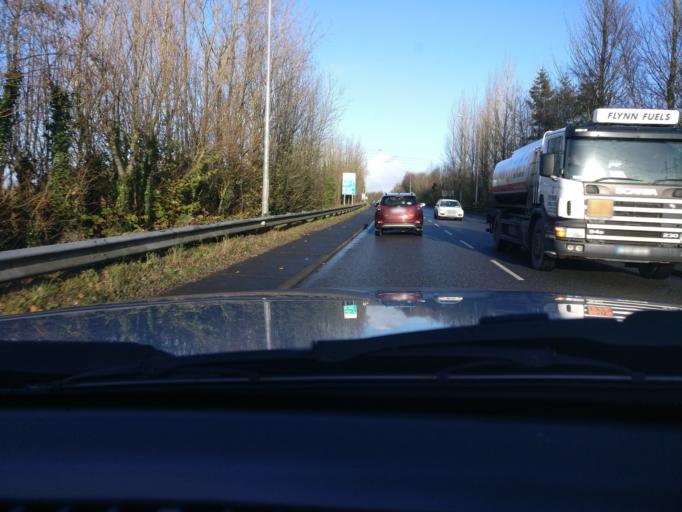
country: IE
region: Leinster
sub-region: An Iarmhi
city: An Muileann gCearr
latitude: 53.5471
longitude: -7.3340
